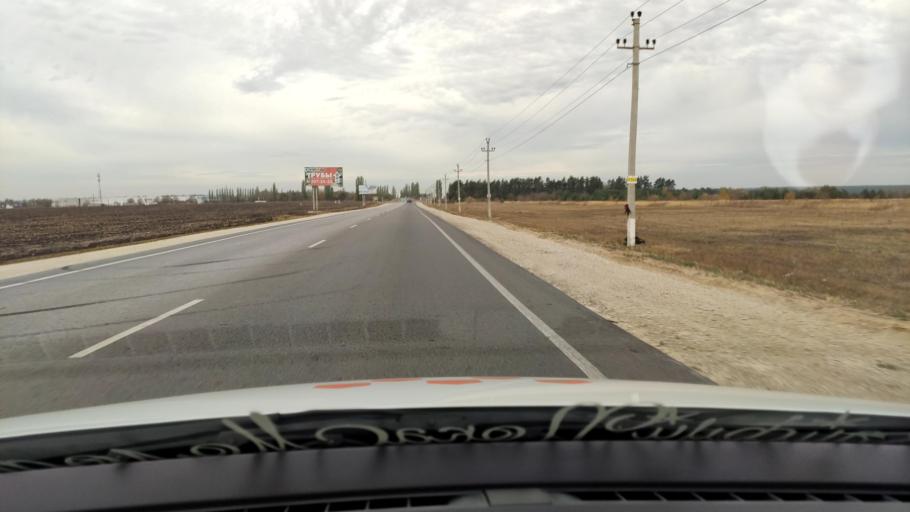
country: RU
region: Voronezj
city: Ramon'
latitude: 51.9289
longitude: 39.2326
